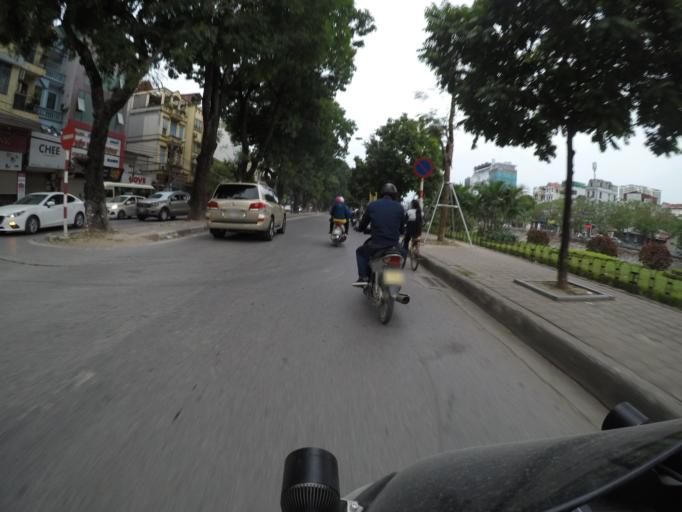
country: VN
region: Ha Noi
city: Cau Giay
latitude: 21.0235
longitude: 105.7989
